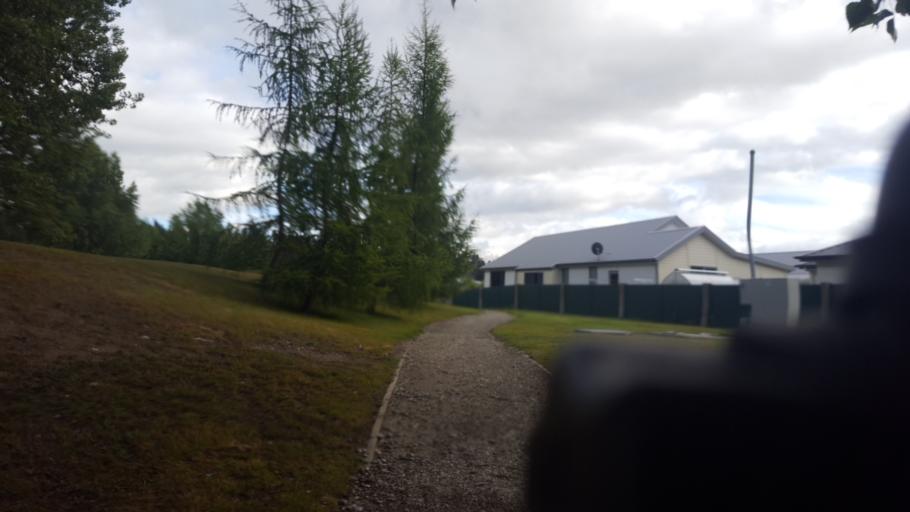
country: NZ
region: Otago
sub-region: Queenstown-Lakes District
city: Wanaka
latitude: -45.2422
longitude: 169.3777
